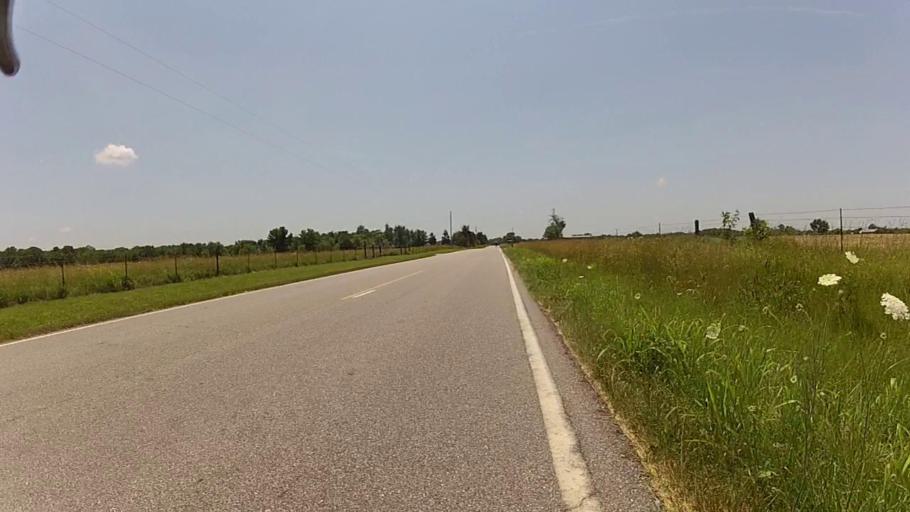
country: US
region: Kansas
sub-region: Montgomery County
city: Cherryvale
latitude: 37.2248
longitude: -95.5382
